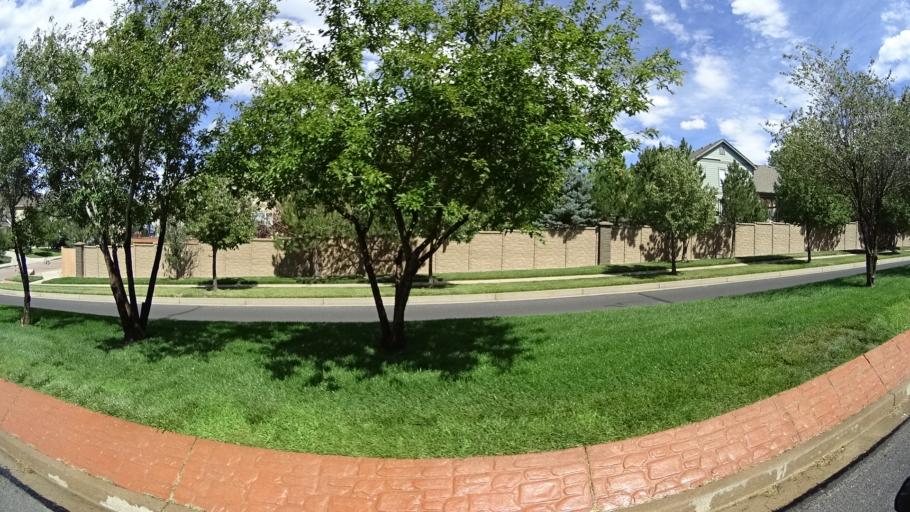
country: US
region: Colorado
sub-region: El Paso County
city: Gleneagle
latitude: 39.0309
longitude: -104.8166
